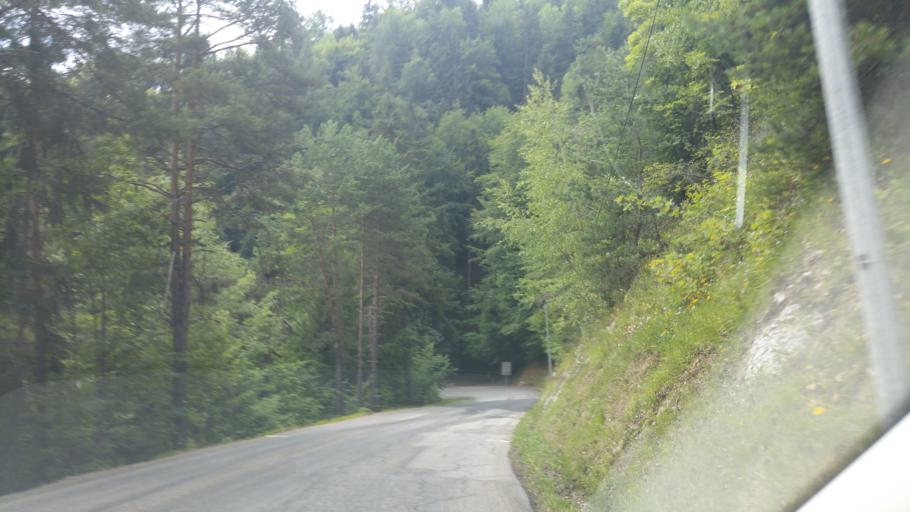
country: FR
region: Rhone-Alpes
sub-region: Departement de la Savoie
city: Saint-Jean-de-Maurienne
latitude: 45.2293
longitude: 6.3066
